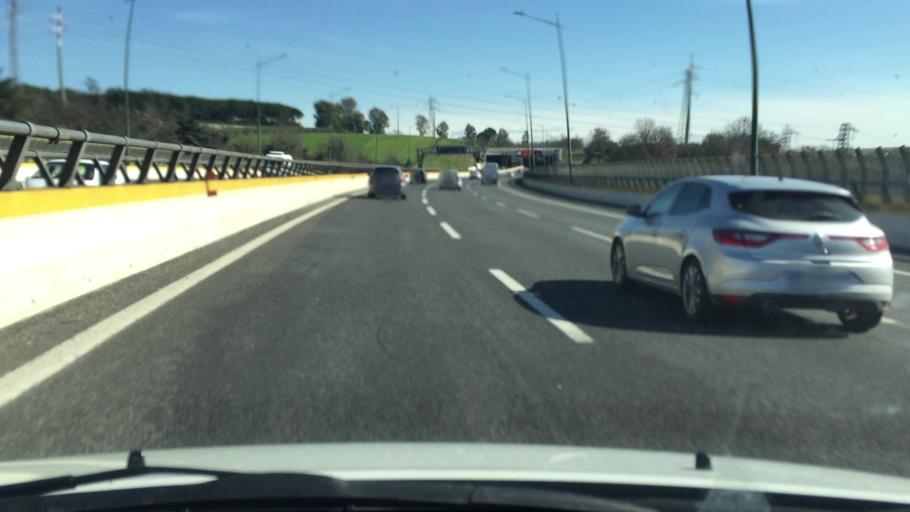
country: VA
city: Vatican City
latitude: 41.9821
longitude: 12.4446
